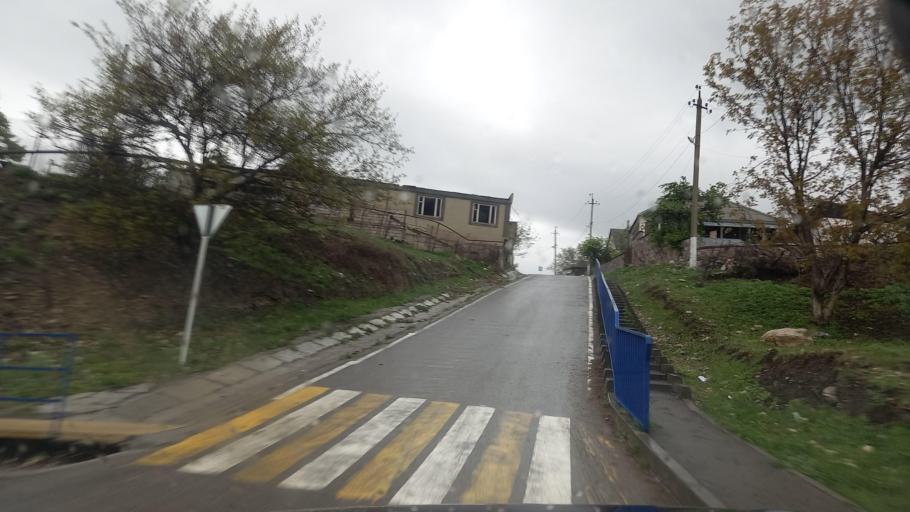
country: RU
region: Kabardino-Balkariya
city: Gundelen
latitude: 43.5971
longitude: 43.1527
